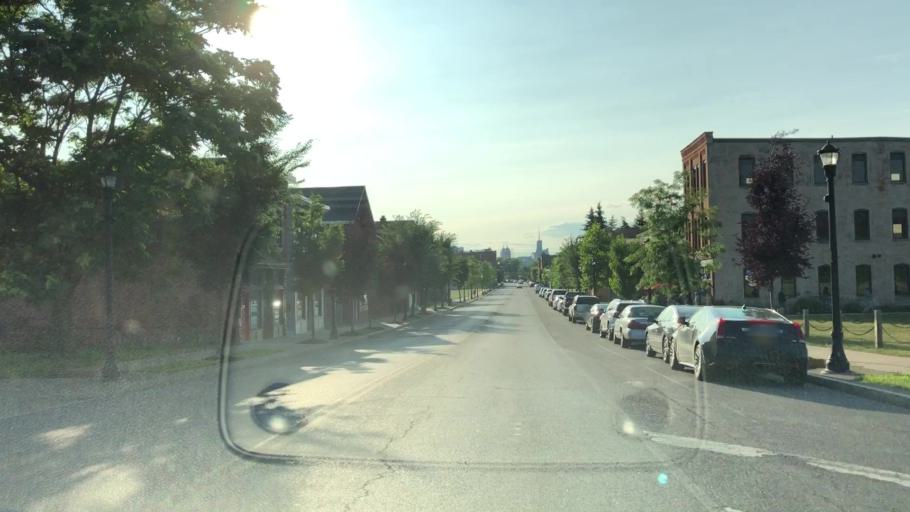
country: US
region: New York
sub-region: Erie County
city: Buffalo
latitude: 42.8746
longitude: -78.8448
